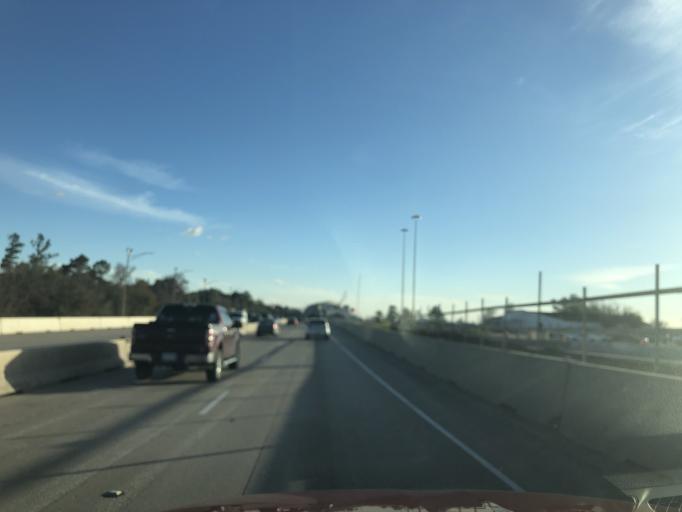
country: US
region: Texas
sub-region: Harris County
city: Cloverleaf
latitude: 29.7518
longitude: -95.1463
